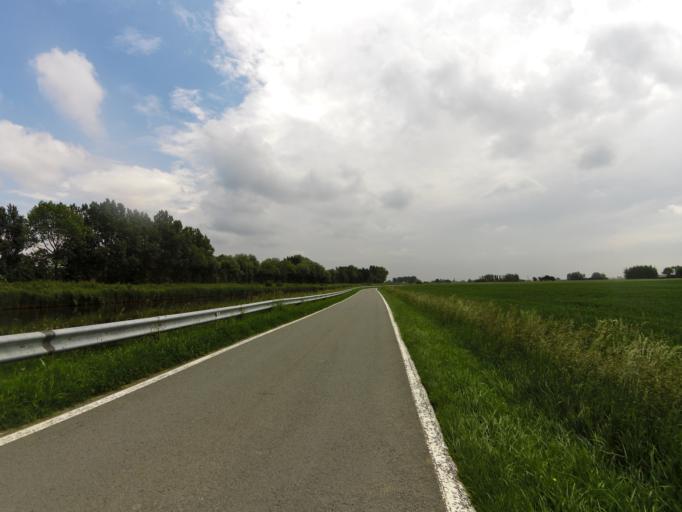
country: BE
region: Flanders
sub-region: Provincie West-Vlaanderen
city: Nieuwpoort
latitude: 51.1252
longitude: 2.8032
